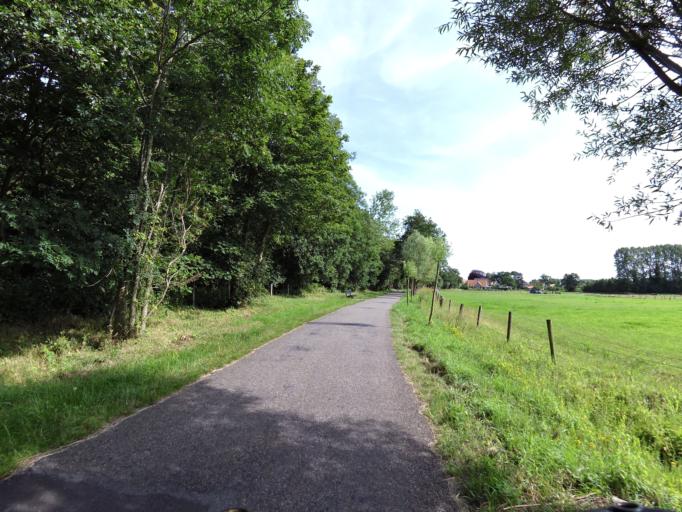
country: NL
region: Zeeland
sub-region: Schouwen-Duiveland
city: Haamstede
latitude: 51.6969
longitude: 3.7352
